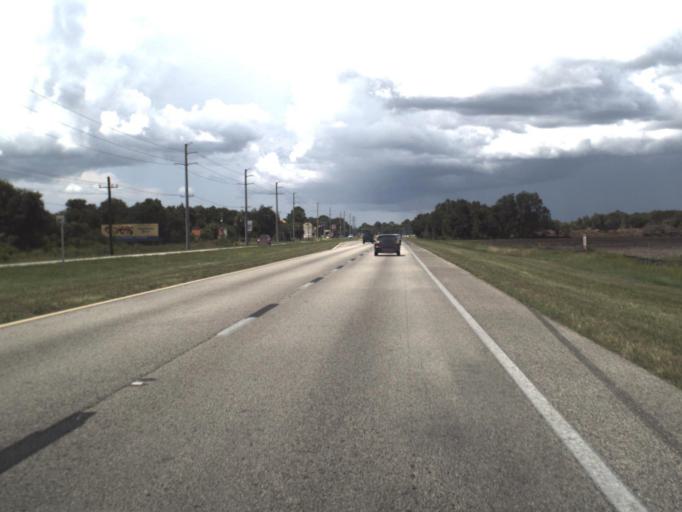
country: US
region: Florida
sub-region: Sarasota County
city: North Port
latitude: 27.0276
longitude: -82.1973
